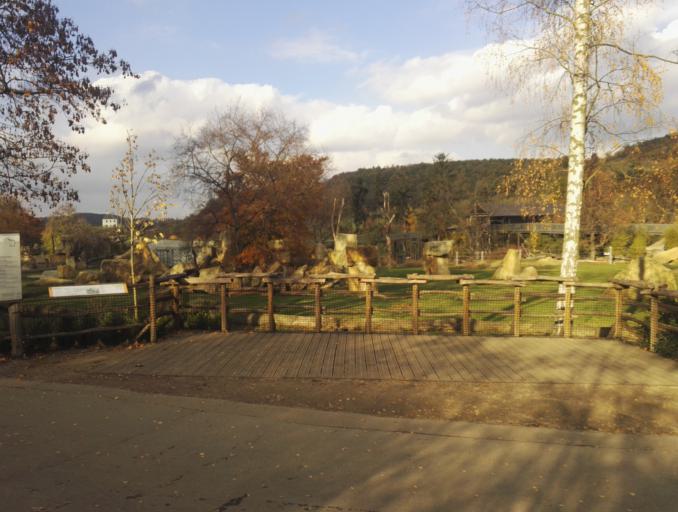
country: CZ
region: Praha
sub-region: Praha 1
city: Mala Strana
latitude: 50.1184
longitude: 14.4066
